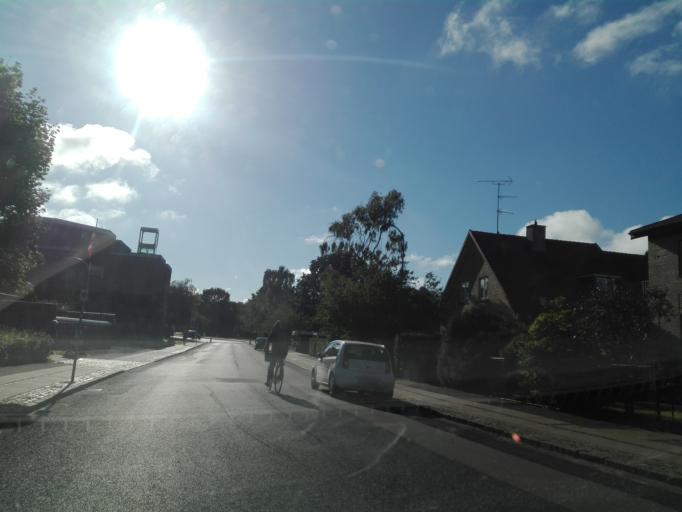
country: DK
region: Capital Region
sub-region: Lyngby-Tarbaek Kommune
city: Kongens Lyngby
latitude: 55.7477
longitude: 12.5204
